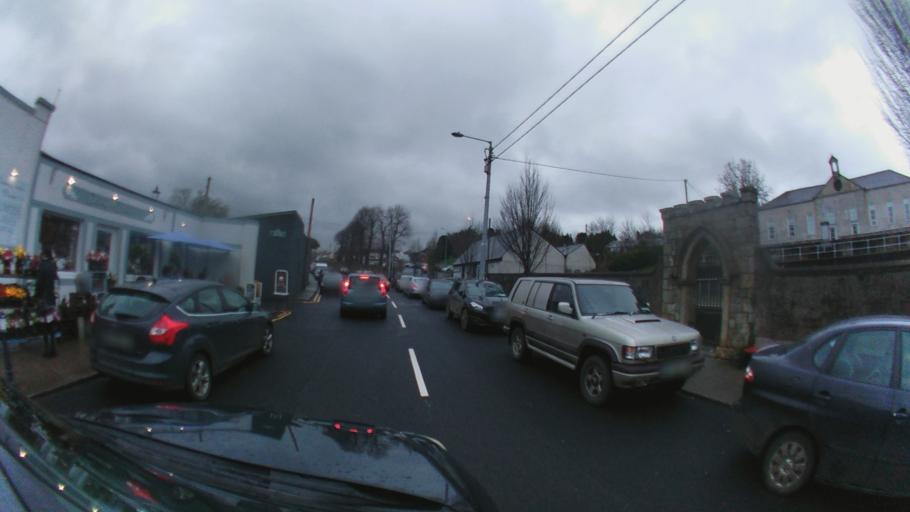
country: IE
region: Leinster
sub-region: Kilkenny
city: Graiguenamanagh
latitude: 52.5420
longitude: -6.9561
